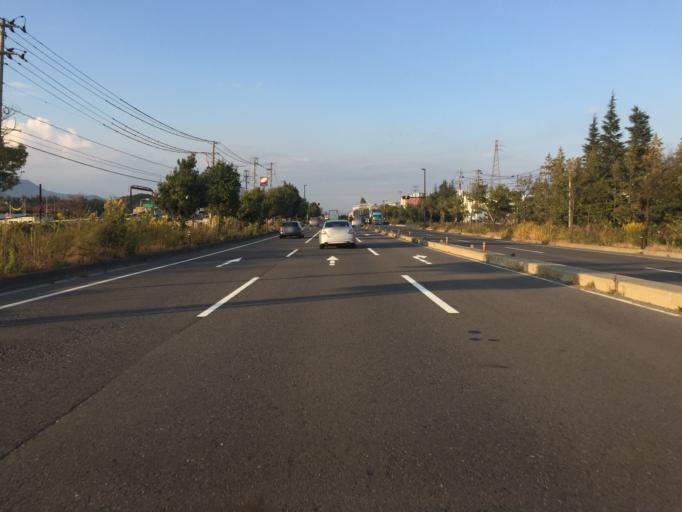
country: JP
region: Fukushima
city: Motomiya
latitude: 37.4730
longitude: 140.3781
